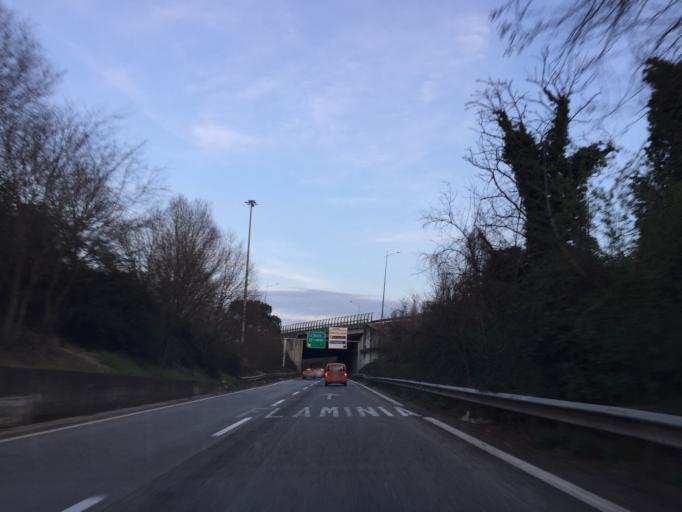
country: IT
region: Latium
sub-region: Citta metropolitana di Roma Capitale
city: Monte Caminetto
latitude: 41.9869
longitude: 12.4731
